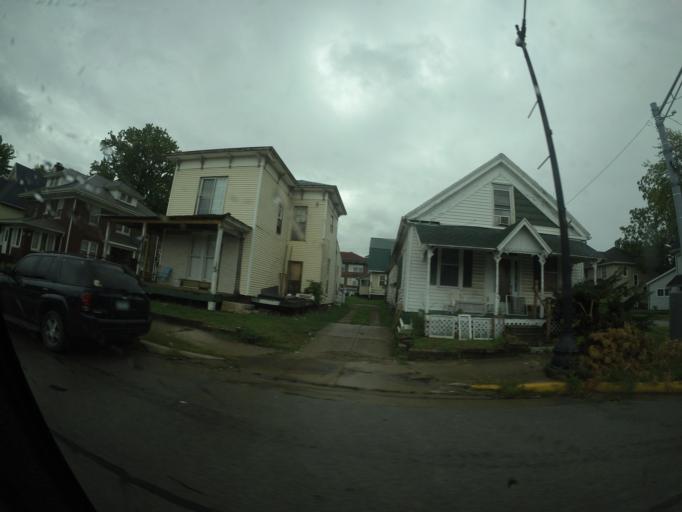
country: US
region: Indiana
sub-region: Montgomery County
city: Crawfordsville
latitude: 40.0372
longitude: -86.9013
